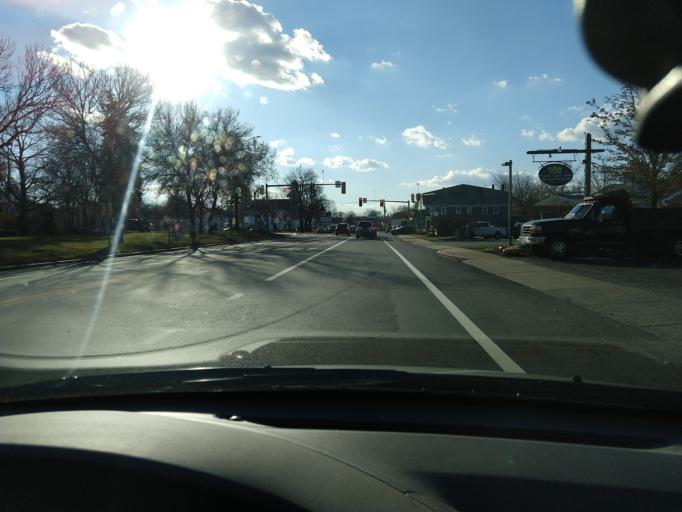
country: US
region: Massachusetts
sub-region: Middlesex County
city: Littleton Common
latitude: 42.5469
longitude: -71.4722
